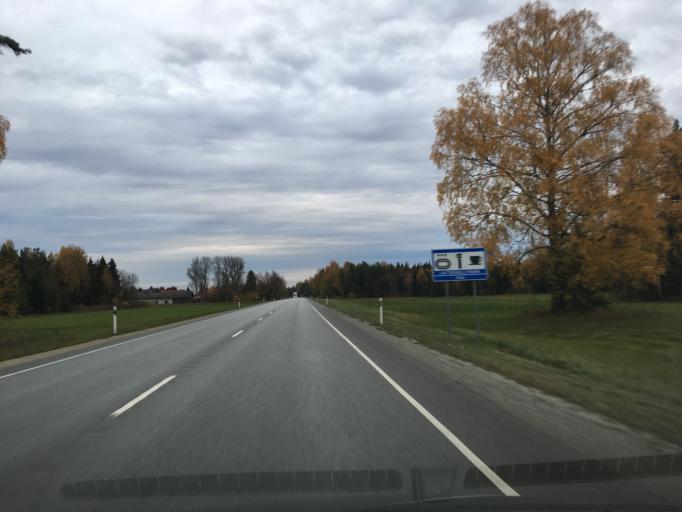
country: EE
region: Harju
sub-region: Nissi vald
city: Riisipere
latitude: 59.1463
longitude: 24.3345
